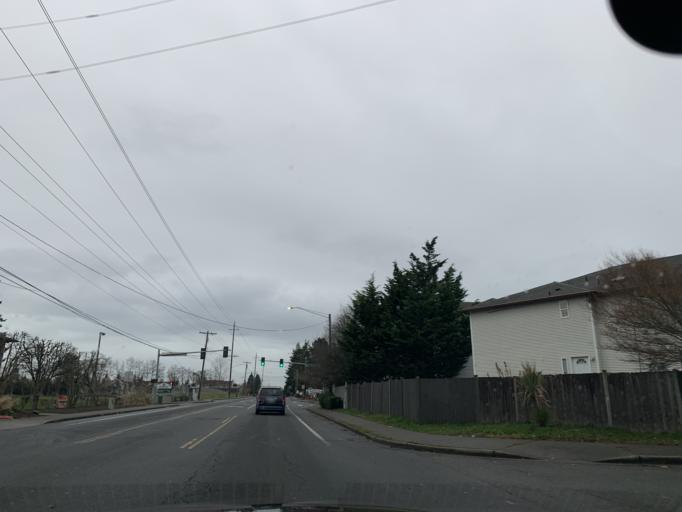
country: US
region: Washington
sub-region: Snohomish County
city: Mukilteo
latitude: 47.9218
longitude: -122.2490
